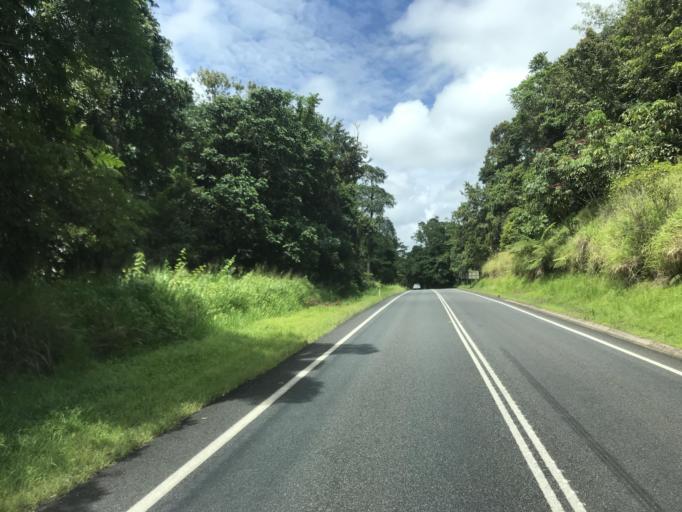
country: AU
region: Queensland
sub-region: Tablelands
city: Ravenshoe
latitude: -17.5923
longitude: 145.7379
